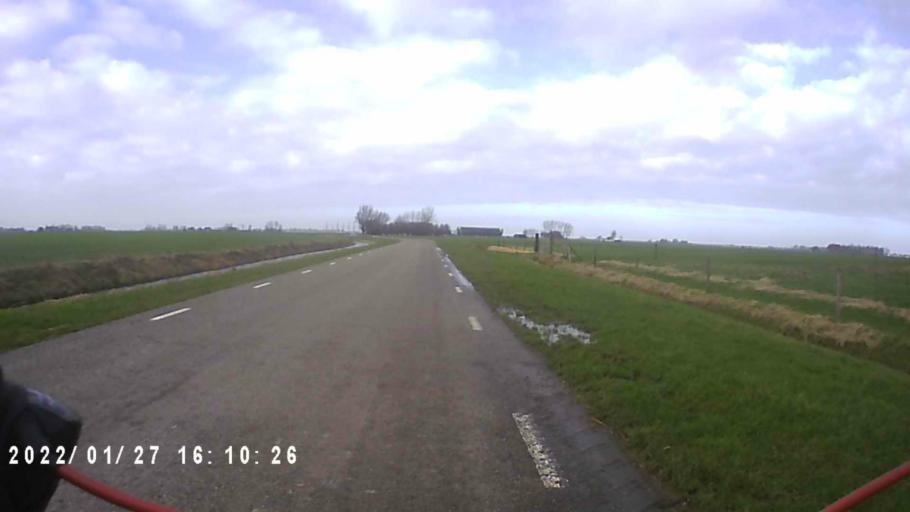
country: NL
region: Friesland
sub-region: Gemeente Dongeradeel
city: Anjum
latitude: 53.3819
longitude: 6.0805
